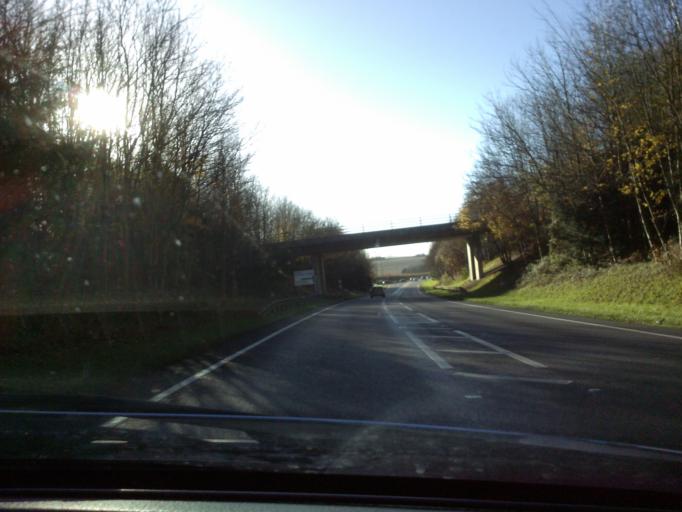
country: GB
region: England
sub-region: Dorset
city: Dorchester
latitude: 50.7083
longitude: -2.4206
